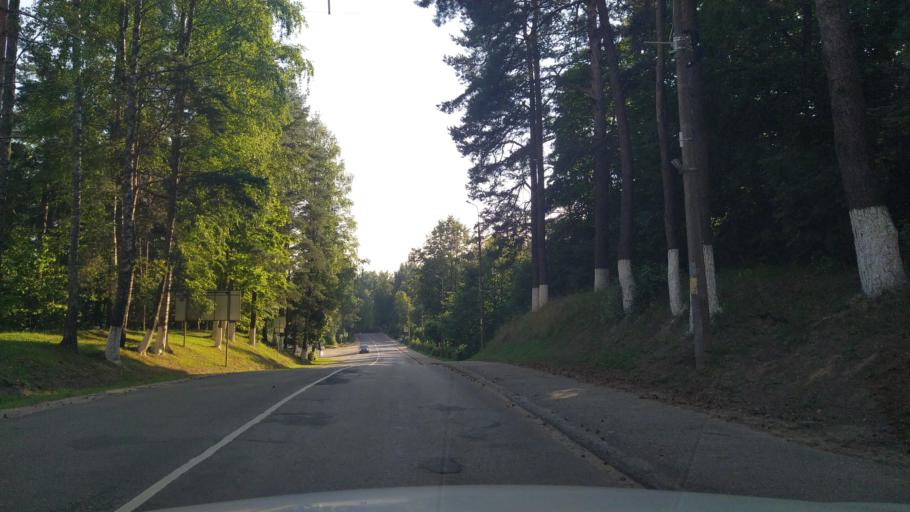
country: RU
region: Pskov
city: Pushkinskiye Gory
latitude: 57.0250
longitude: 28.9255
